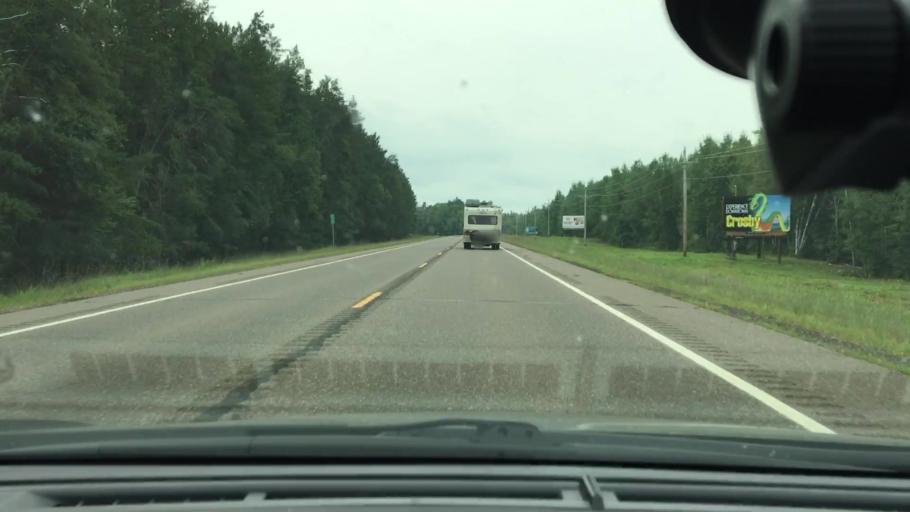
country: US
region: Minnesota
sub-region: Crow Wing County
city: Crosby
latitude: 46.5004
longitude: -93.9572
